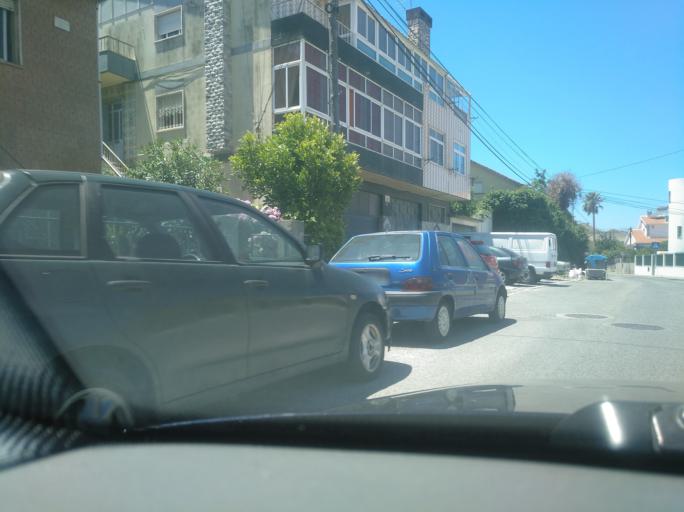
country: PT
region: Lisbon
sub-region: Odivelas
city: Canecas
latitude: 38.8073
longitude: -9.2253
